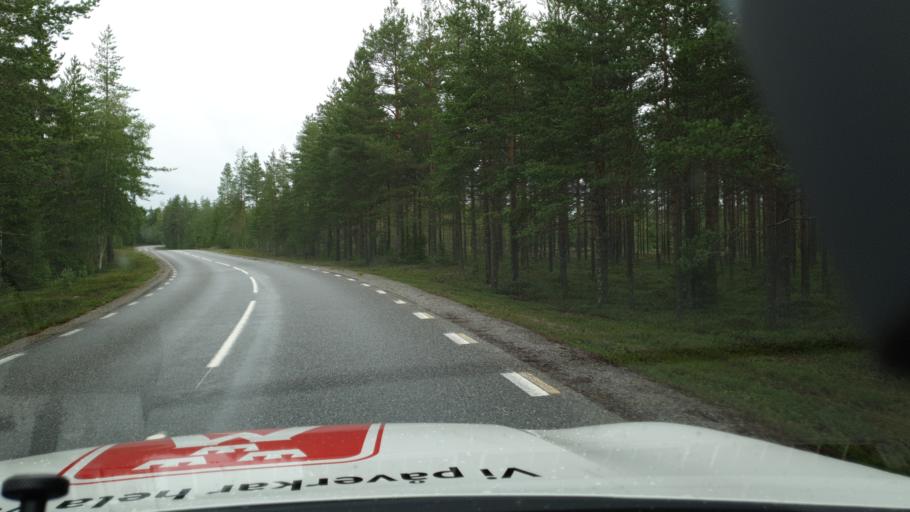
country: SE
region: Vaesterbotten
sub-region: Umea Kommun
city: Saevar
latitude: 64.0177
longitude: 20.4898
